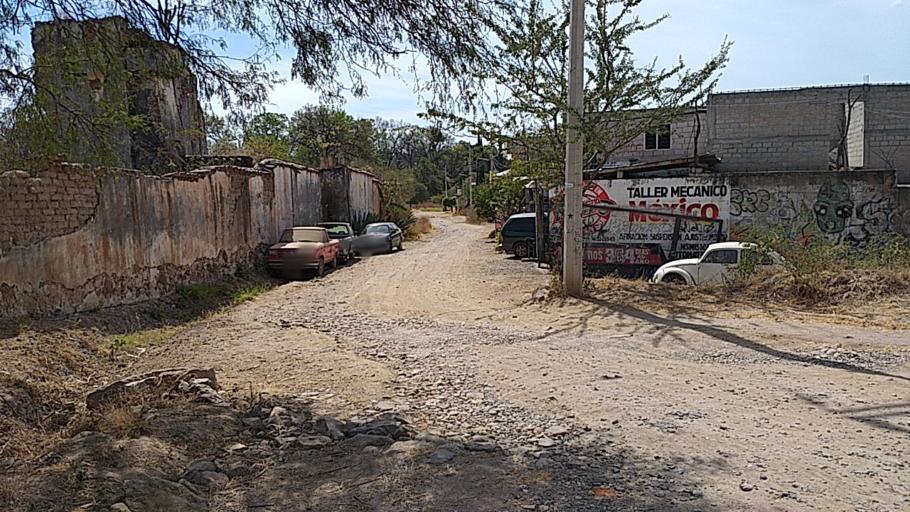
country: MX
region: Oaxaca
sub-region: Heroica Ciudad de Huajuapan de Leon
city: Vista Hermosa
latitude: 17.8126
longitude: -97.7624
